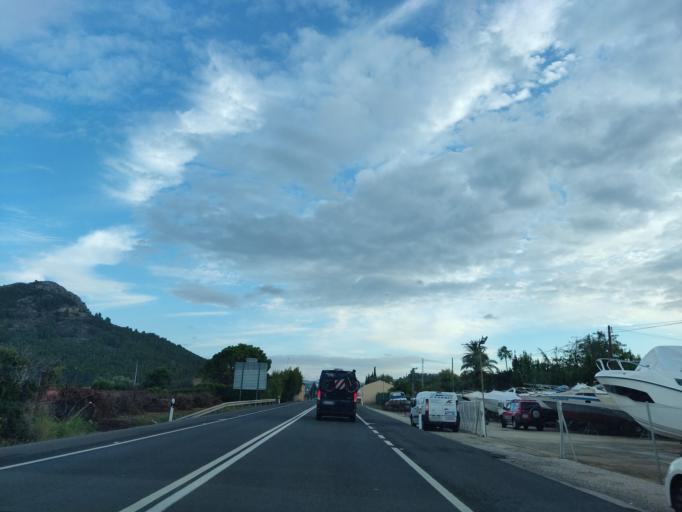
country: ES
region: Valencia
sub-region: Provincia de Alicante
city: Pedreguer
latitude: 38.8127
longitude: 0.0307
